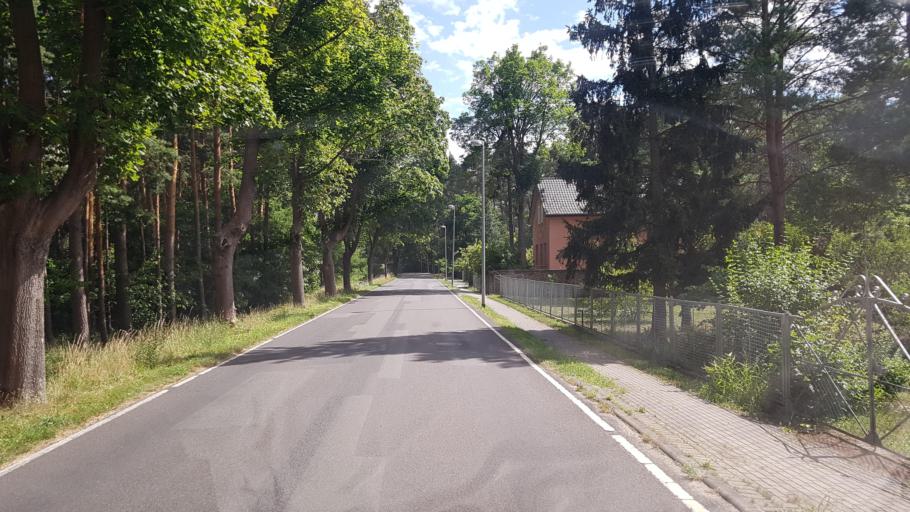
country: DE
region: Brandenburg
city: Luckenwalde
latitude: 52.1219
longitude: 13.1895
